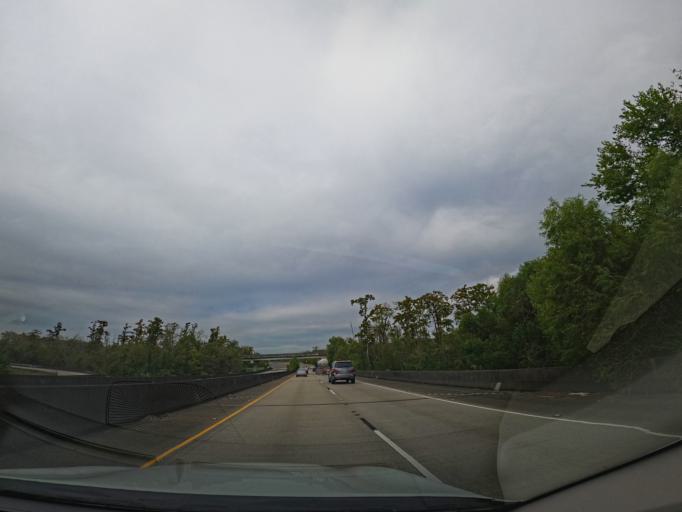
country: US
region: Louisiana
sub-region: Saint Mary Parish
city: Amelia
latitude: 29.6712
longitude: -91.1082
